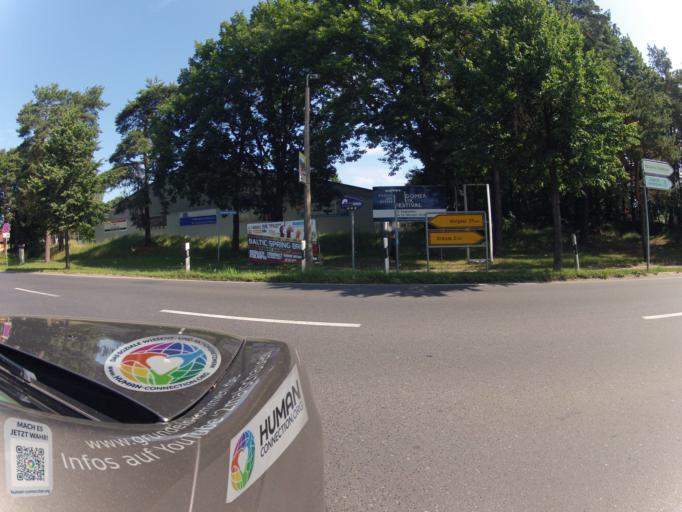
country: DE
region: Mecklenburg-Vorpommern
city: Seebad Heringsdorf
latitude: 53.9342
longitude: 14.1930
